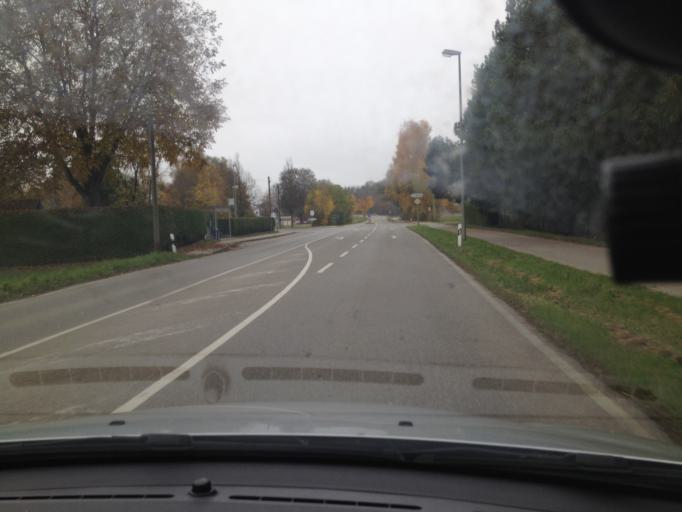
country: DE
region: Bavaria
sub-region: Swabia
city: Schwabmunchen
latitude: 48.1754
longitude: 10.7363
